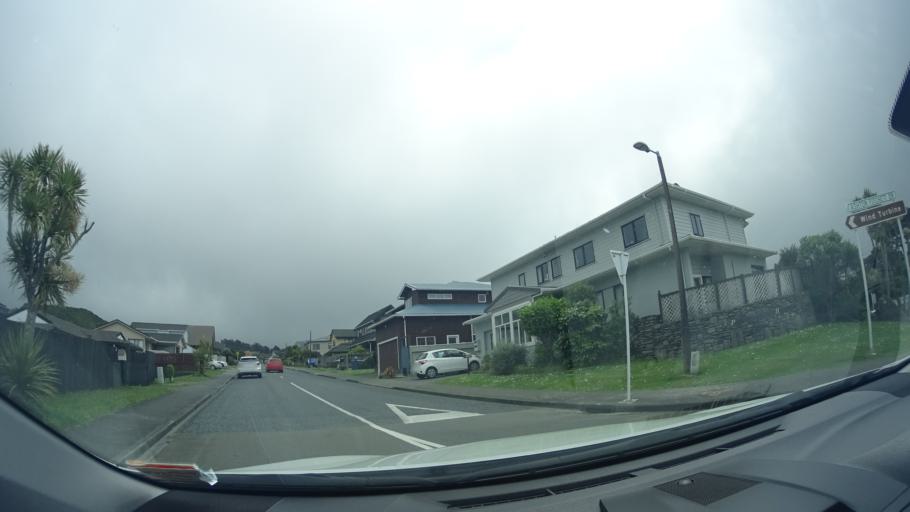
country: NZ
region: Wellington
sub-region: Wellington City
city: Brooklyn
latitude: -41.3044
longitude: 174.7579
